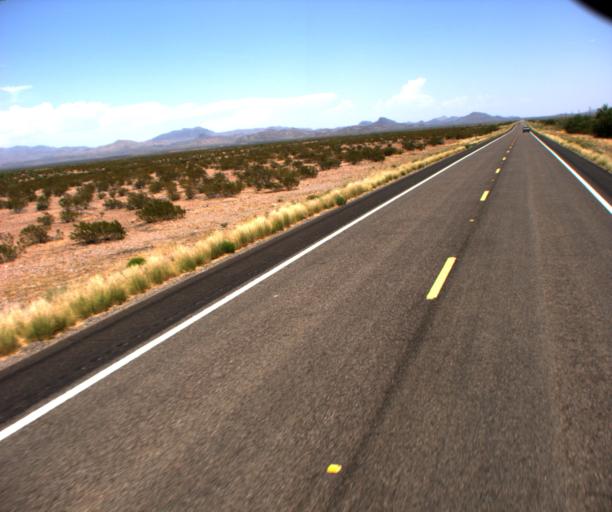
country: US
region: Arizona
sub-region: Graham County
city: Safford
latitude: 32.7801
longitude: -109.5258
